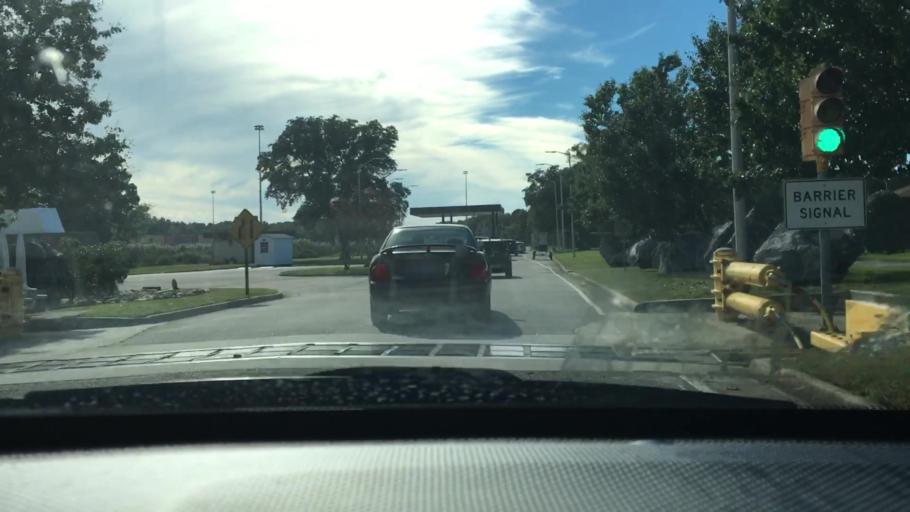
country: US
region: Virginia
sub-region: City of Portsmouth
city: Portsmouth Heights
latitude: 36.8811
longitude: -76.3593
